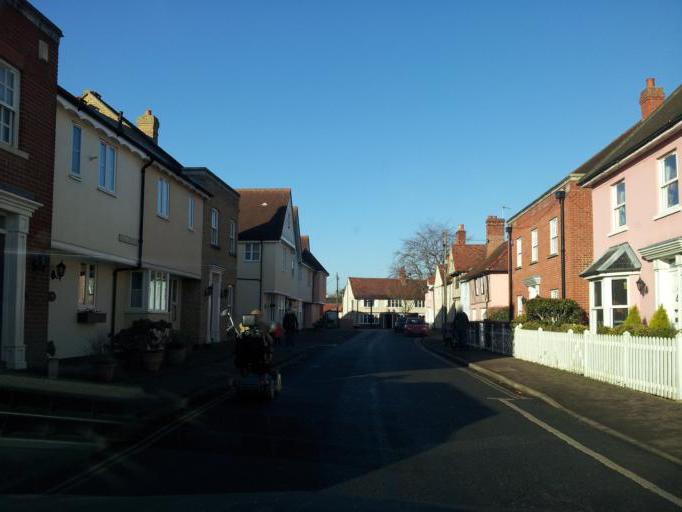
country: GB
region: England
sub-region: Suffolk
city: Sudbury
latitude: 51.9714
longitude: 0.7766
